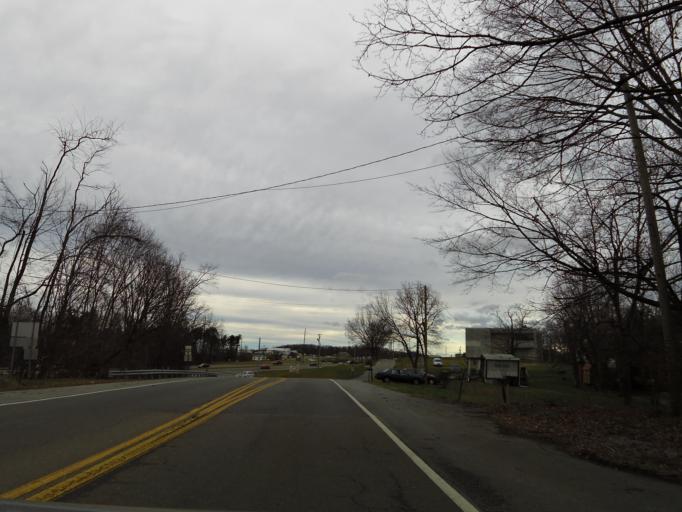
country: US
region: Tennessee
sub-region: Greene County
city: Greeneville
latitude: 36.1772
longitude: -82.8232
